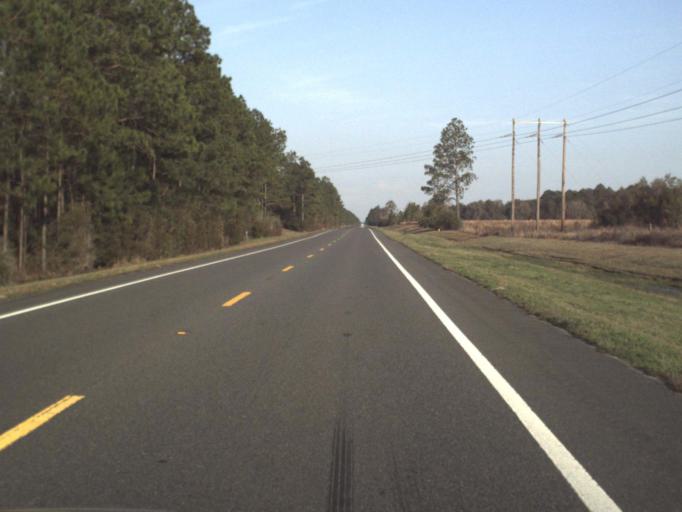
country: US
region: Florida
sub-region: Bay County
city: Lynn Haven
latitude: 30.4397
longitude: -85.7850
